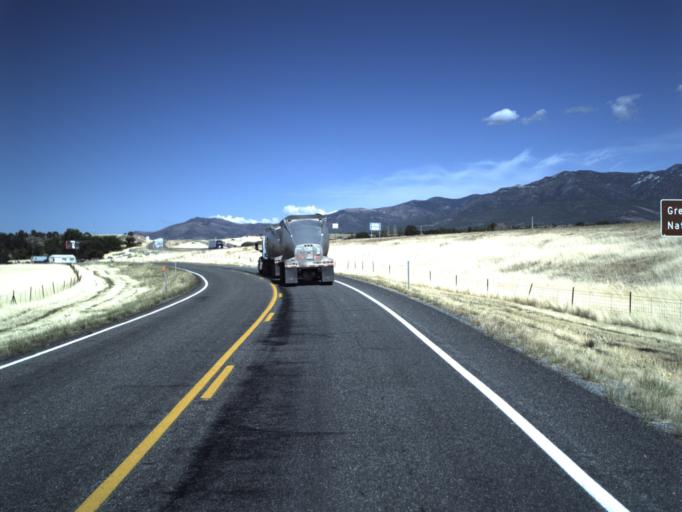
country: US
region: Utah
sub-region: Millard County
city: Fillmore
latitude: 39.0851
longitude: -112.2763
